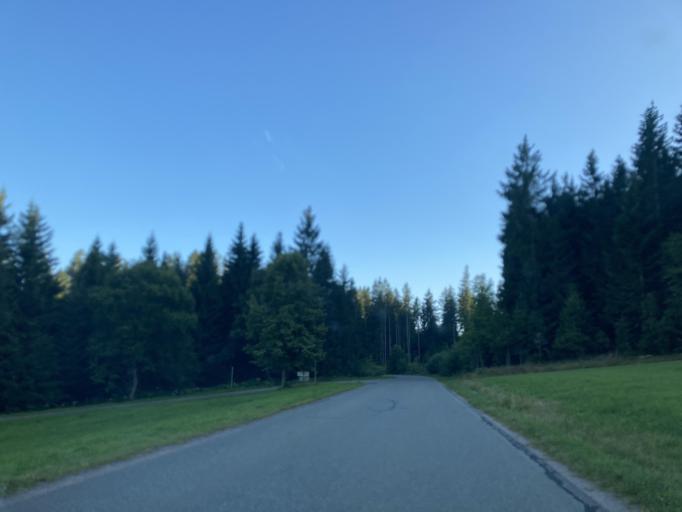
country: DE
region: Baden-Wuerttemberg
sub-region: Freiburg Region
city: Schonach im Schwarzwald
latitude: 48.1572
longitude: 8.1857
